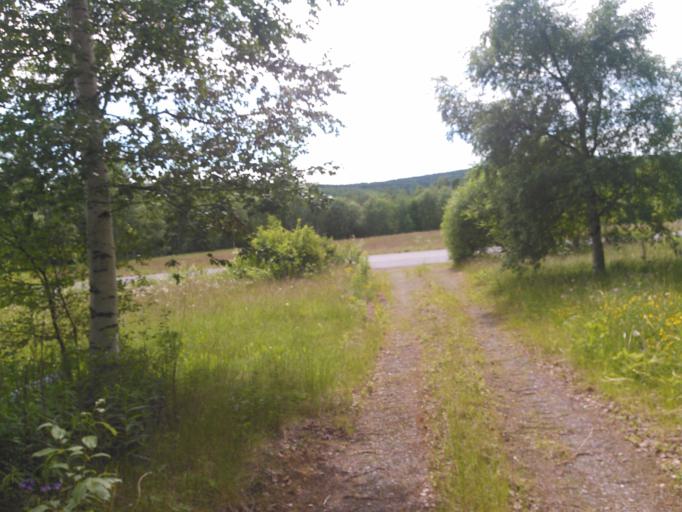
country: SE
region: Vaesterbotten
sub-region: Vannas Kommun
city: Vannasby
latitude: 63.8924
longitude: 19.9830
